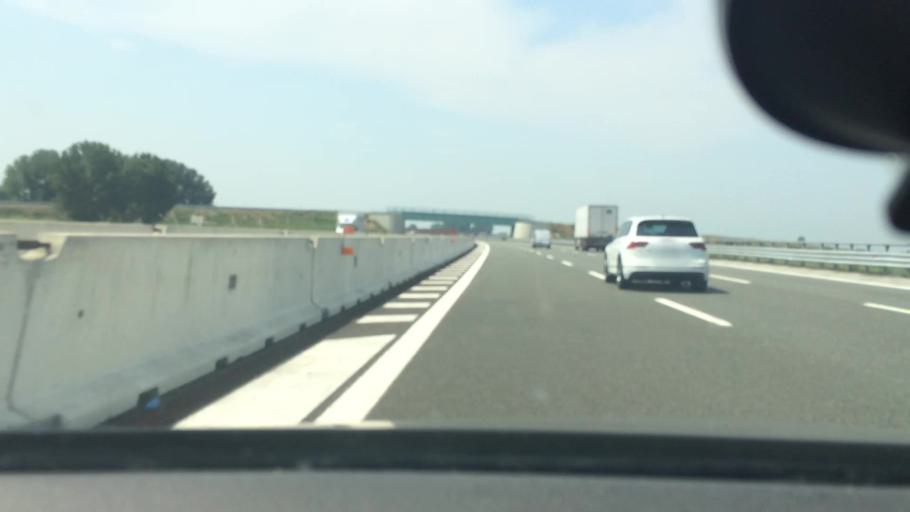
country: IT
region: Lombardy
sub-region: Provincia di Lodi
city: Cassino d'Alberi
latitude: 45.3990
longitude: 9.3886
